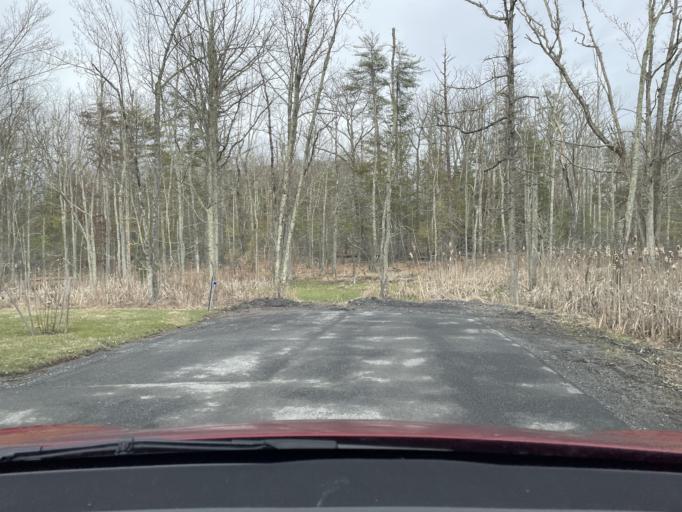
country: US
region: New York
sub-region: Ulster County
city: Woodstock
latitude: 42.0276
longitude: -74.1028
